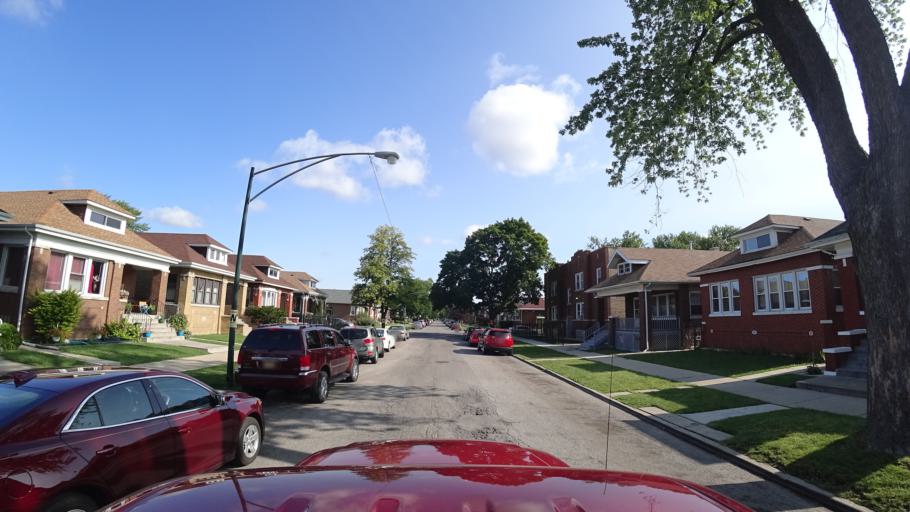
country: US
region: Illinois
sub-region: Cook County
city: Hometown
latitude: 41.7876
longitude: -87.6961
